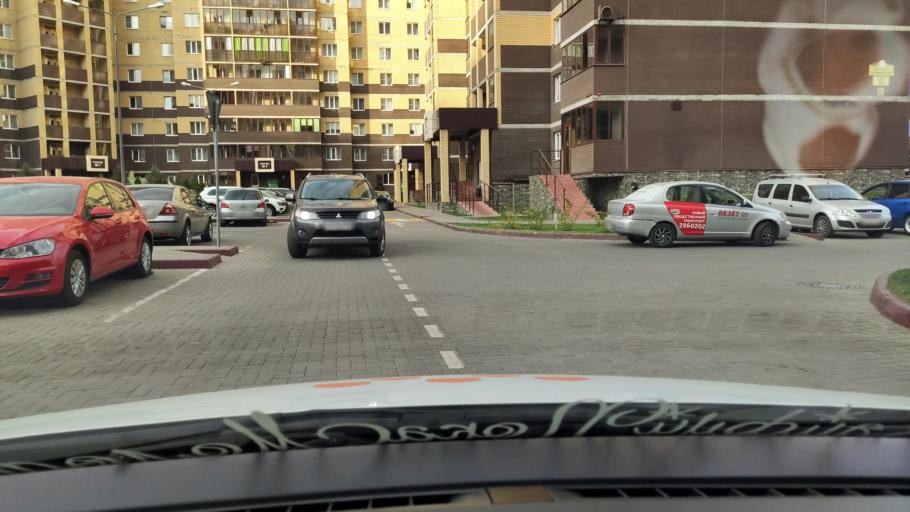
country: RU
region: Voronezj
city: Voronezh
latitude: 51.7140
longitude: 39.1976
